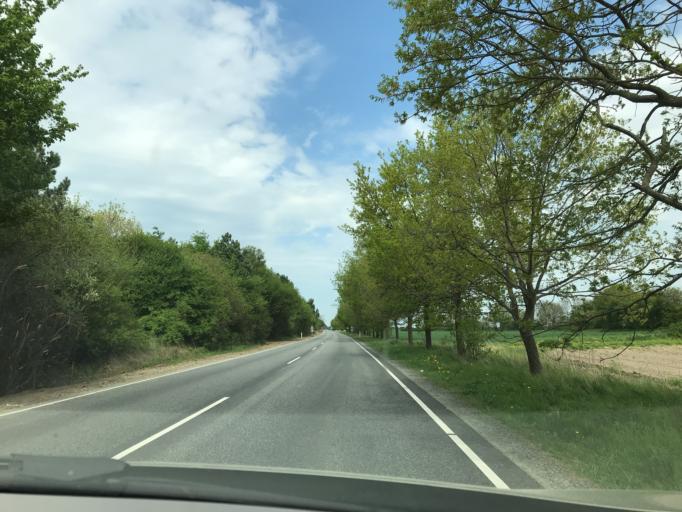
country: DK
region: South Denmark
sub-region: Assens Kommune
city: Assens
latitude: 55.2744
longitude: 9.9205
